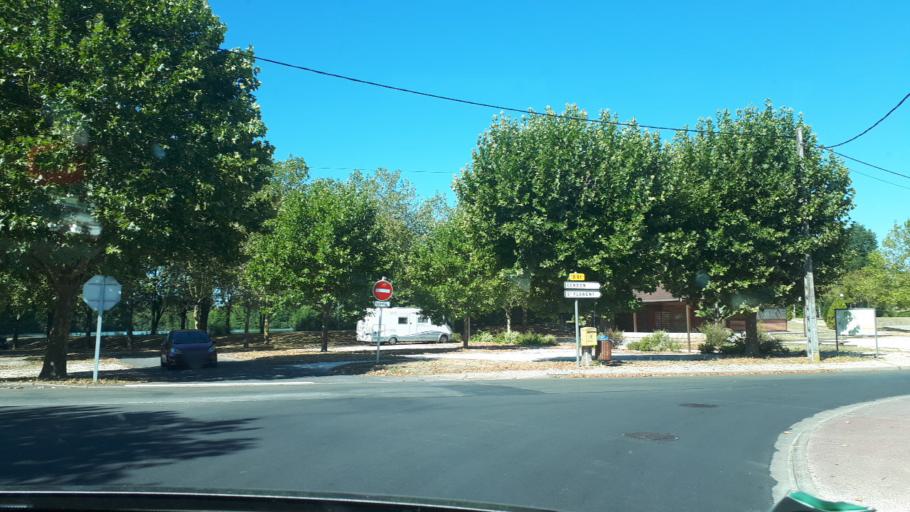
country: FR
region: Centre
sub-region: Departement du Loiret
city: Coullons
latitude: 47.6236
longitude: 2.4920
